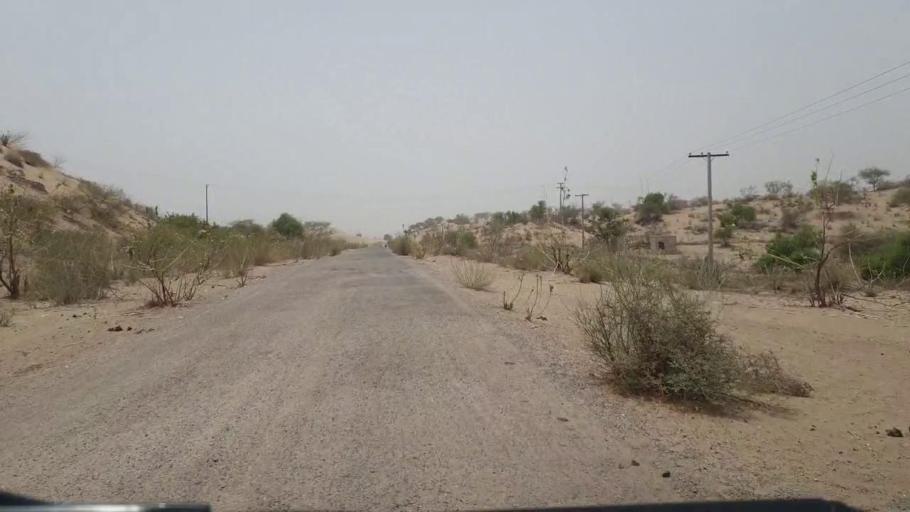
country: PK
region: Sindh
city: Naukot
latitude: 24.7578
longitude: 69.5516
